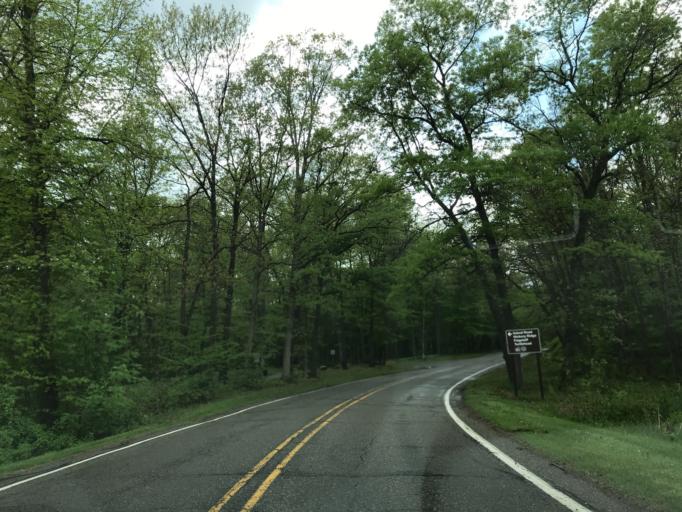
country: US
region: Michigan
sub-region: Oakland County
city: South Lyon
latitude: 42.5329
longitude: -83.6571
